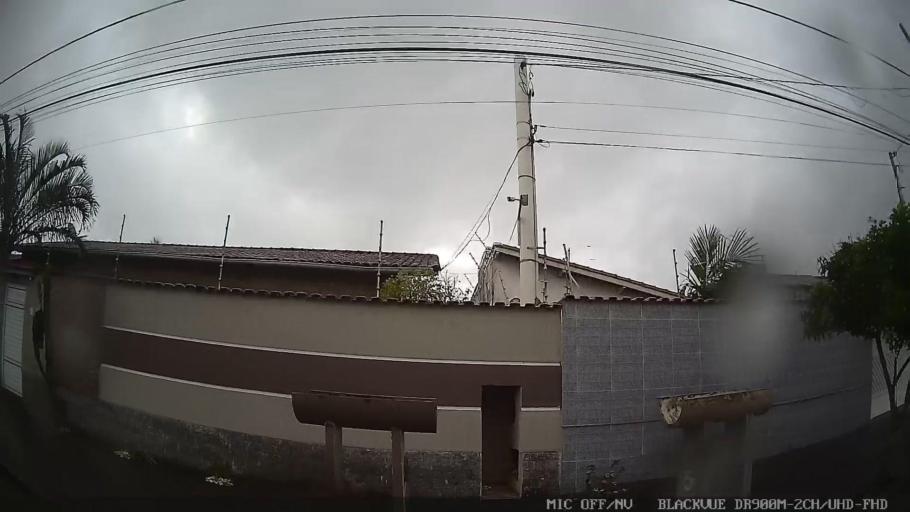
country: BR
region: Sao Paulo
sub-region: Itanhaem
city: Itanhaem
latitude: -24.1719
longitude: -46.7703
